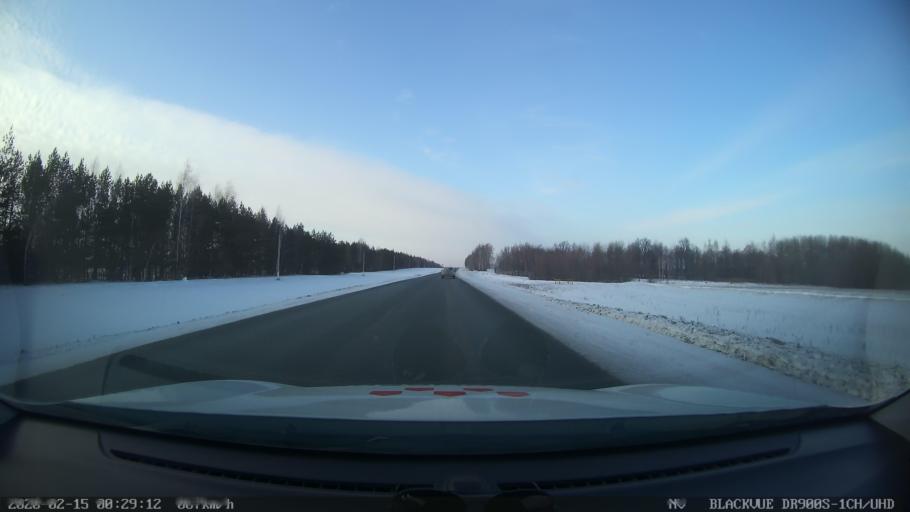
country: RU
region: Tatarstan
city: Verkhniy Uslon
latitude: 55.6487
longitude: 48.8709
